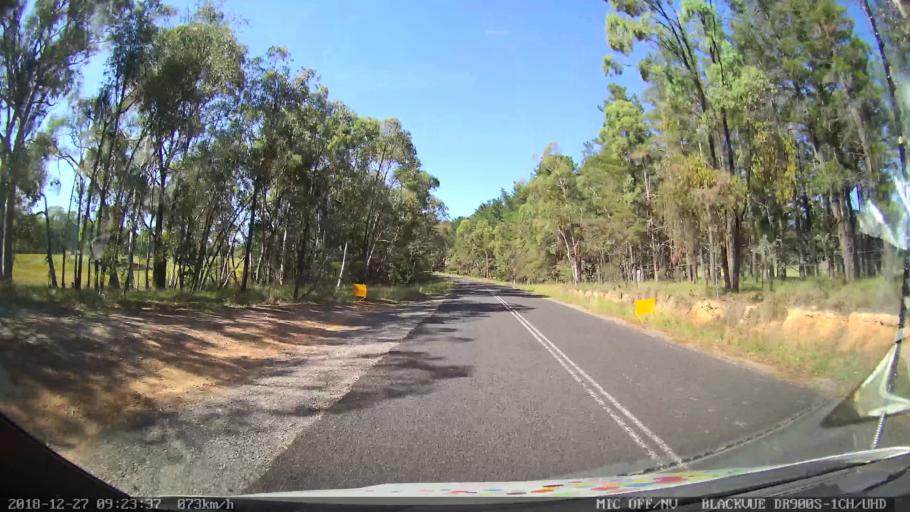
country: AU
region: New South Wales
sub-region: Lithgow
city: Portland
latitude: -33.1277
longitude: 149.9963
